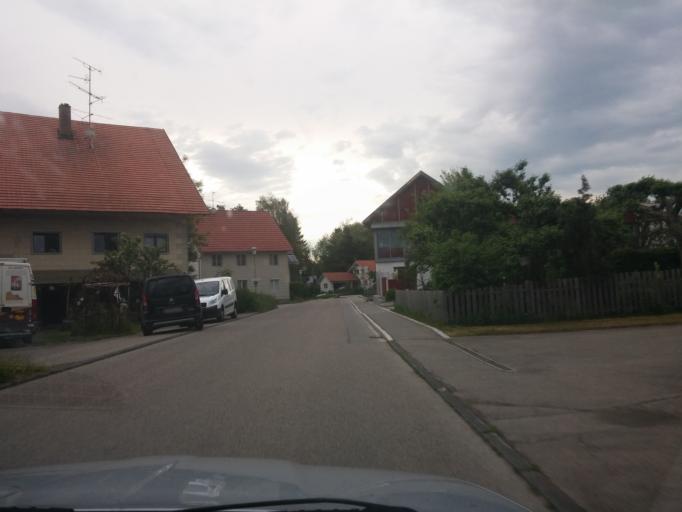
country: DE
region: Bavaria
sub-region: Swabia
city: Legau
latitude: 47.8242
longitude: 10.0988
